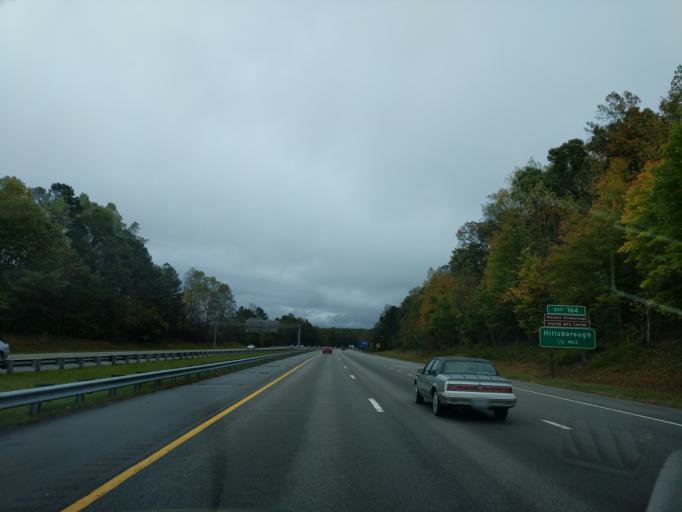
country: US
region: North Carolina
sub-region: Orange County
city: Hillsborough
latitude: 36.0592
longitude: -79.1186
